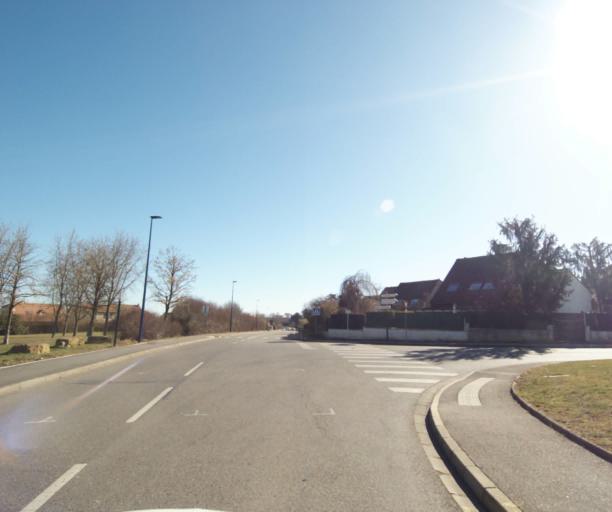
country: FR
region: Lorraine
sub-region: Departement de Meurthe-et-Moselle
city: Ludres
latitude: 48.6179
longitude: 6.1662
